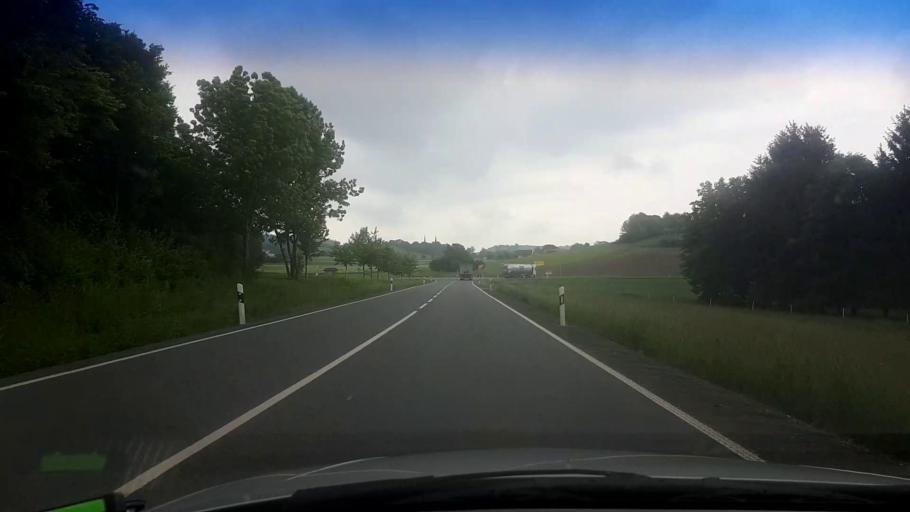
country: DE
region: Bavaria
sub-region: Upper Franconia
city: Goldkronach
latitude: 50.0056
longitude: 11.6791
